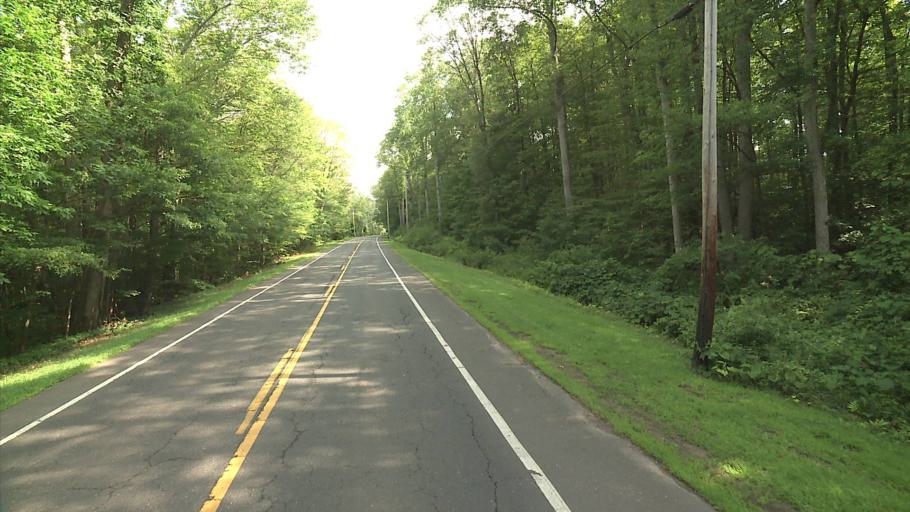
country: US
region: Connecticut
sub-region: Middlesex County
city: Moodus
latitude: 41.5247
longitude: -72.4138
